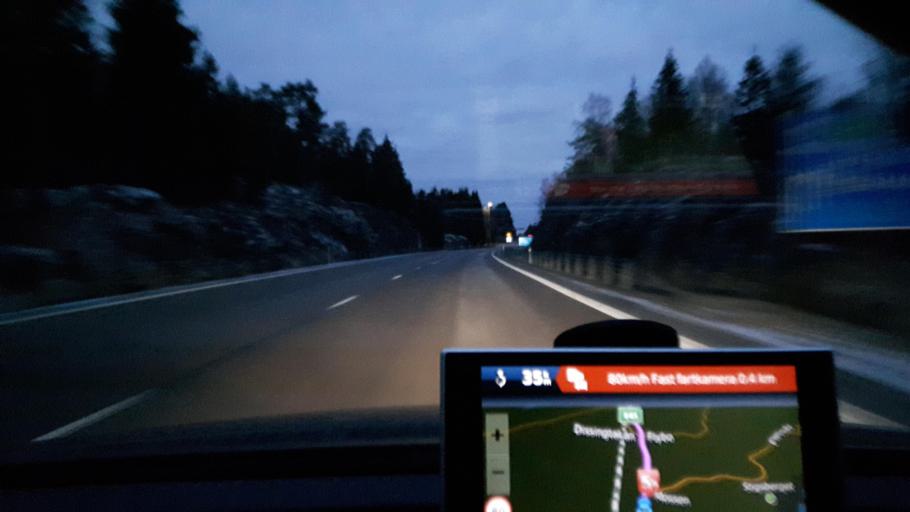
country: SE
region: Vaestra Goetaland
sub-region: Vanersborgs Kommun
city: Vanersborg
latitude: 58.4200
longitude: 12.2907
